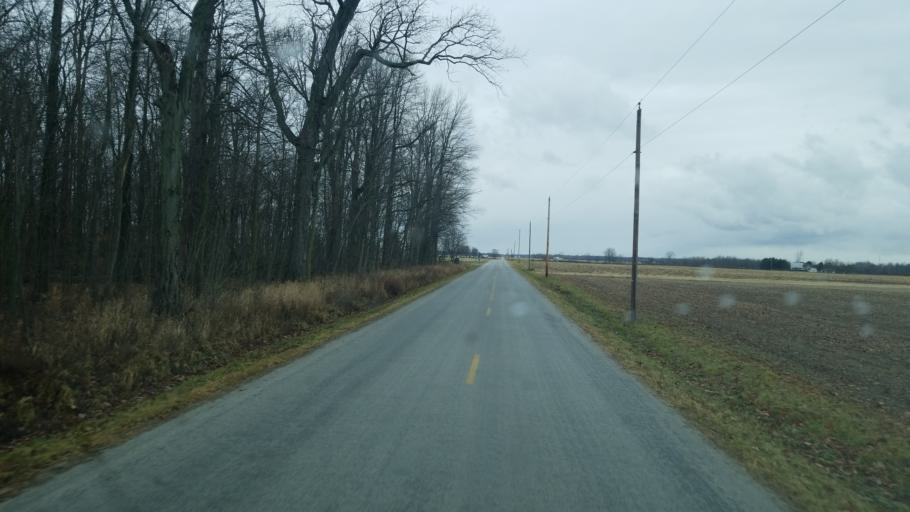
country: US
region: Ohio
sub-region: Hardin County
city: Kenton
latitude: 40.7024
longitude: -83.5648
